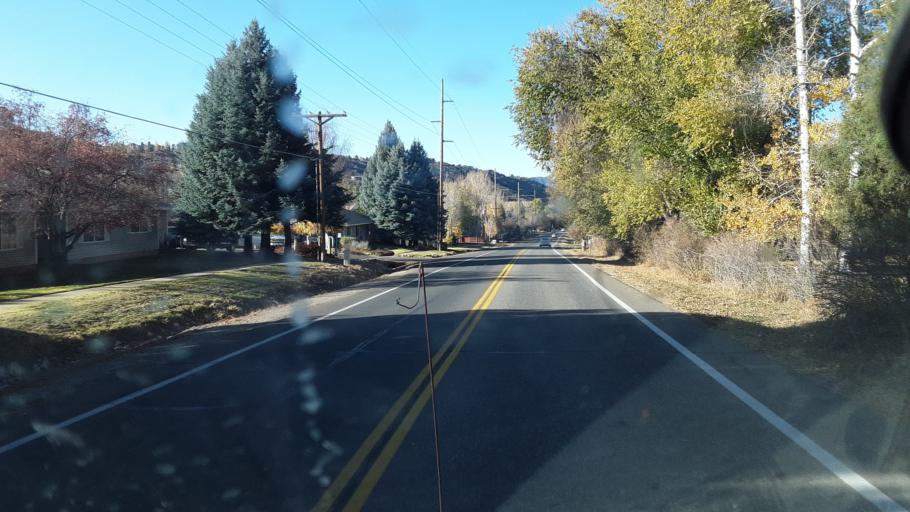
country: US
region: Colorado
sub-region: La Plata County
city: Durango
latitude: 37.3032
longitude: -107.8368
